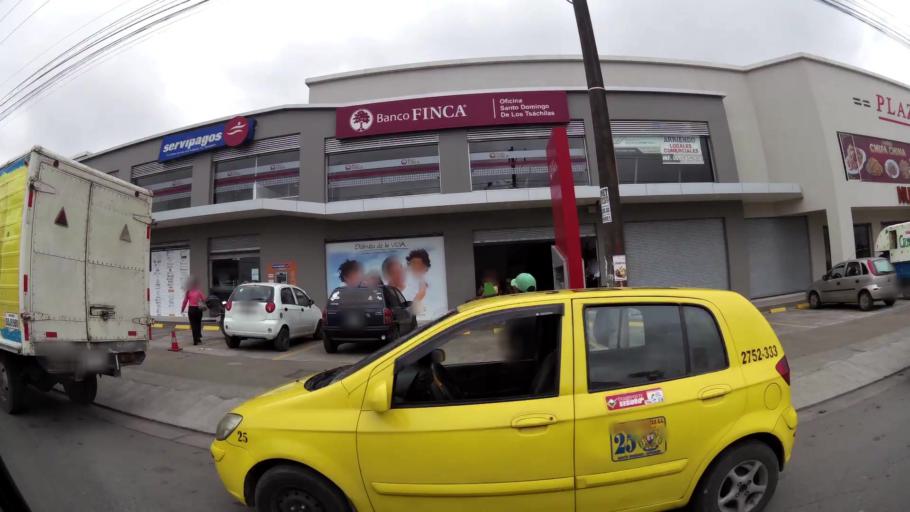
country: EC
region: Santo Domingo de los Tsachilas
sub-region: Canton Santo Domingo de los Colorados
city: Santo Domingo de los Colorados
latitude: -0.2649
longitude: -79.1710
